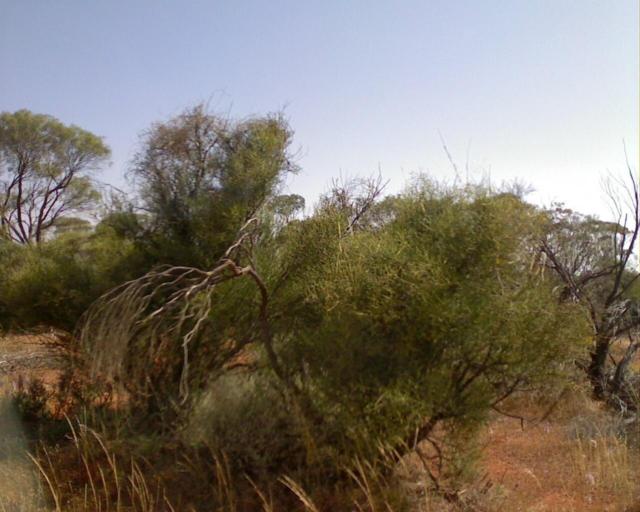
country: AU
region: Western Australia
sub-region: Merredin
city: Merredin
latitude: -30.9574
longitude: 118.8835
